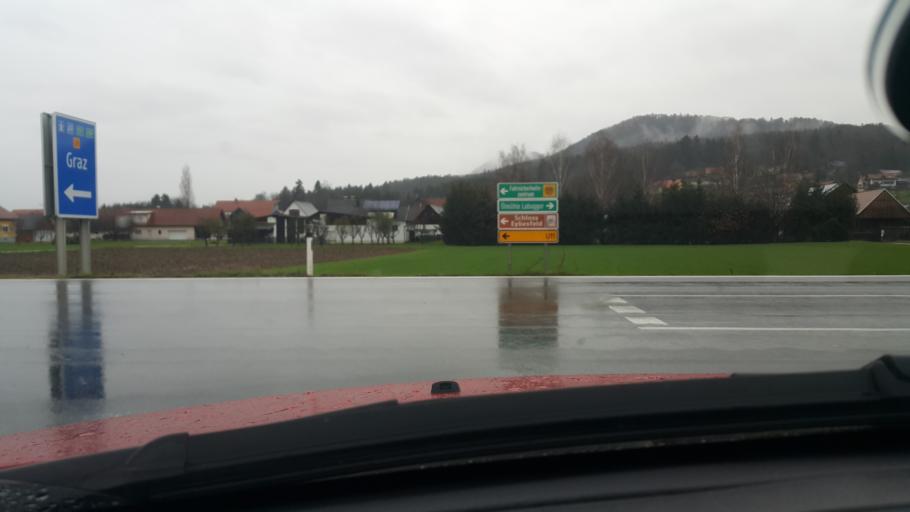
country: AT
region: Styria
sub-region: Politischer Bezirk Leibnitz
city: Lang
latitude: 46.8533
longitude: 15.5168
